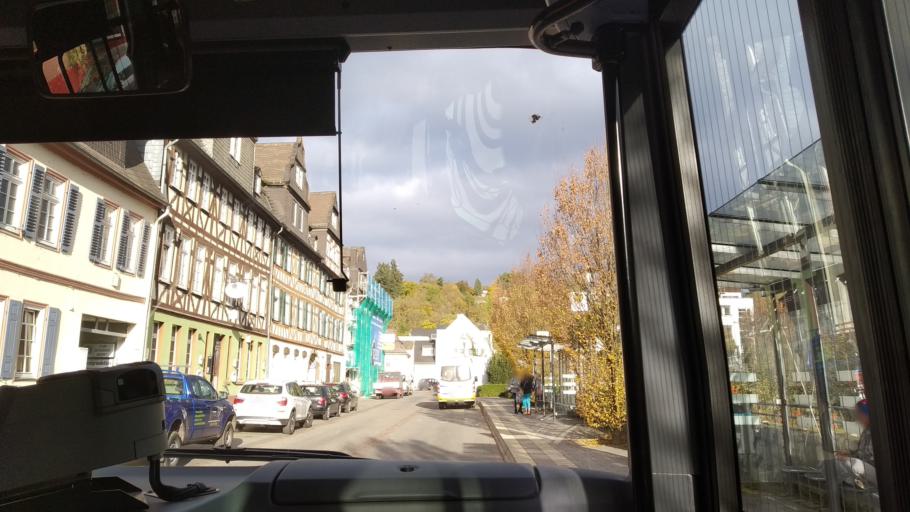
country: DE
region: Rheinland-Pfalz
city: Diez
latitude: 50.3702
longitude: 8.0078
